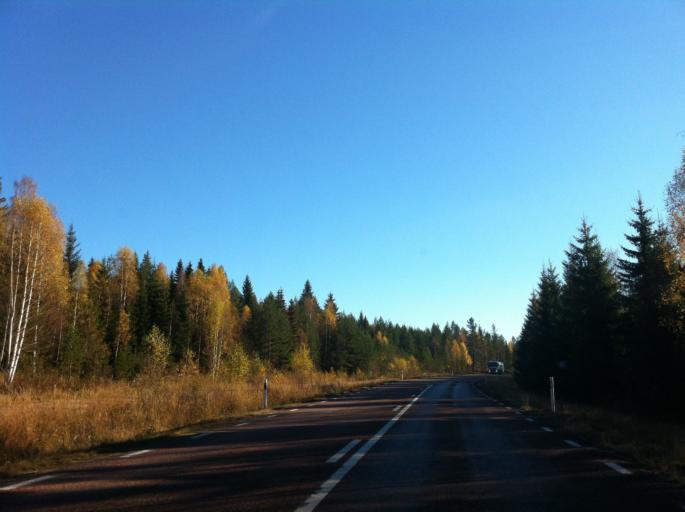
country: SE
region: Dalarna
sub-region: Alvdalens Kommun
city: AElvdalen
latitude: 61.1703
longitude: 14.1059
